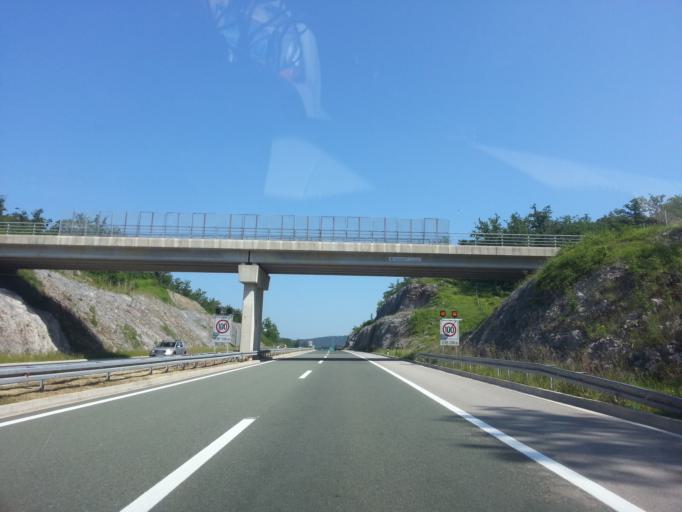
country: HR
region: Primorsko-Goranska
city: Matulji
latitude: 45.4500
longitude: 14.2719
